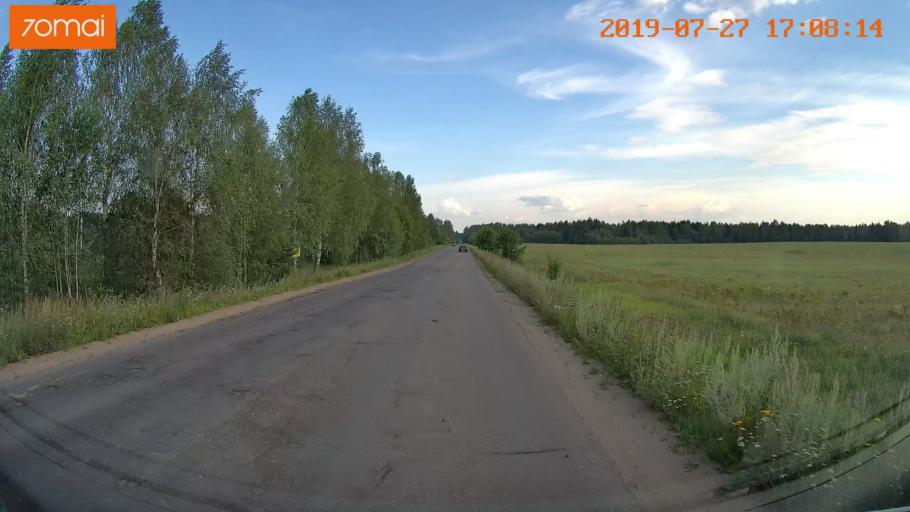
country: RU
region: Ivanovo
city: Novo-Talitsy
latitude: 57.0837
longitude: 40.8360
